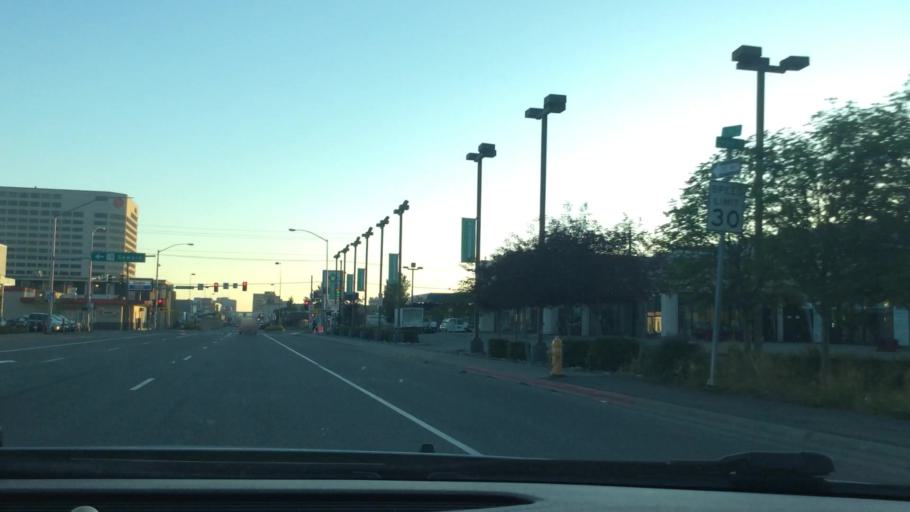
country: US
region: Alaska
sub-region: Anchorage Municipality
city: Anchorage
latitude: 61.2176
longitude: -149.8688
